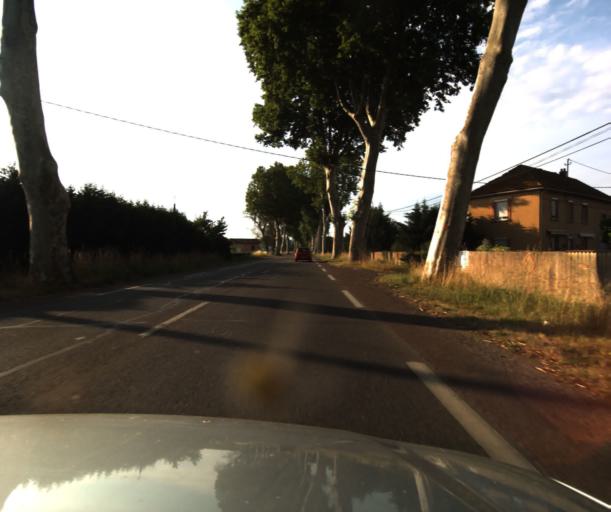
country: FR
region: Midi-Pyrenees
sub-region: Departement du Tarn-et-Garonne
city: Moissac
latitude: 44.0834
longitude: 1.0901
